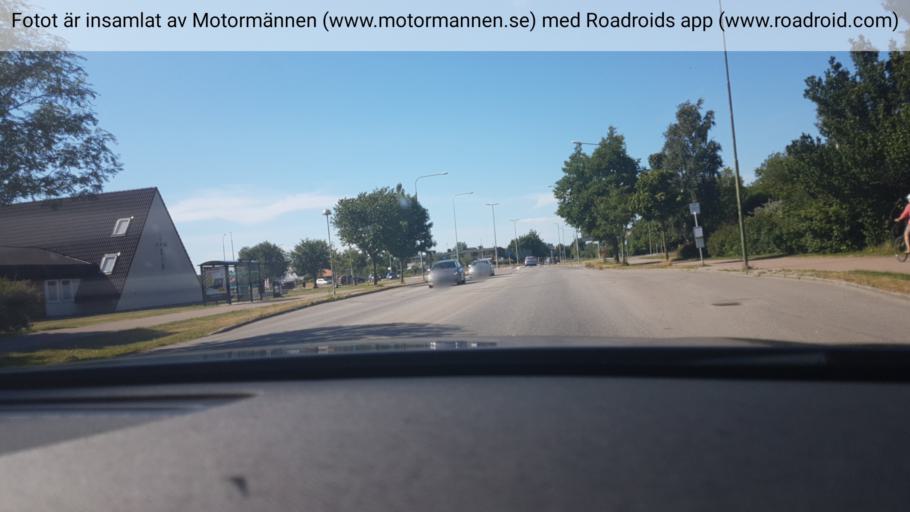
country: SE
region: Halland
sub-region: Falkenbergs Kommun
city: Falkenberg
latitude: 56.8913
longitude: 12.5069
